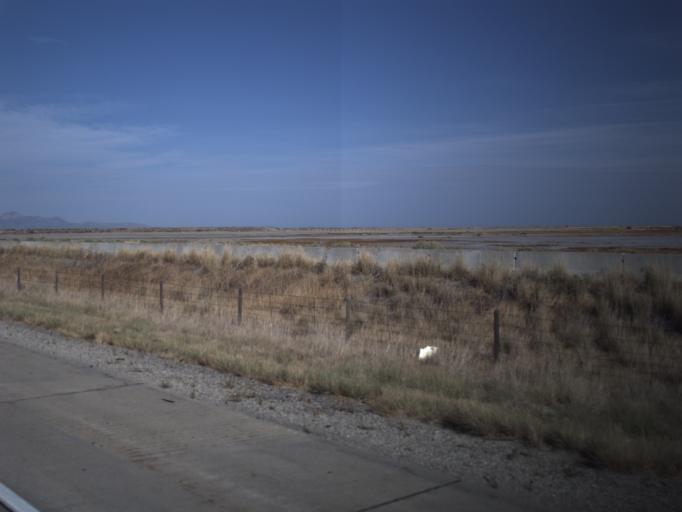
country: US
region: Utah
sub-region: Salt Lake County
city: Magna
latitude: 40.7710
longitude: -112.1277
